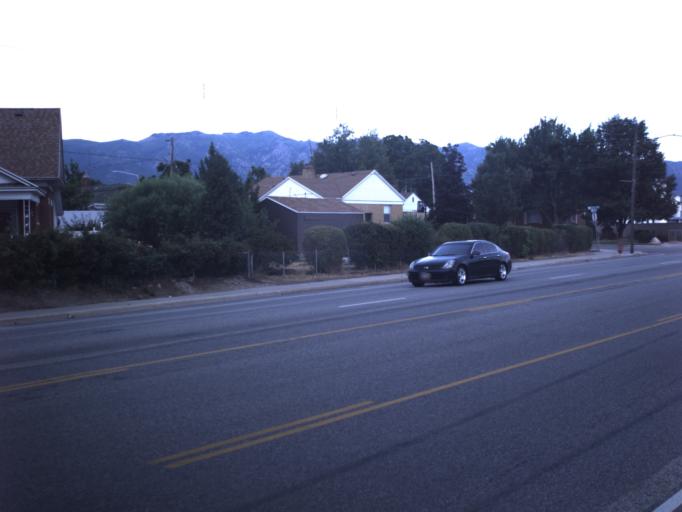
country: US
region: Utah
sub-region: Davis County
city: Clearfield
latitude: 41.1047
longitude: -112.0166
